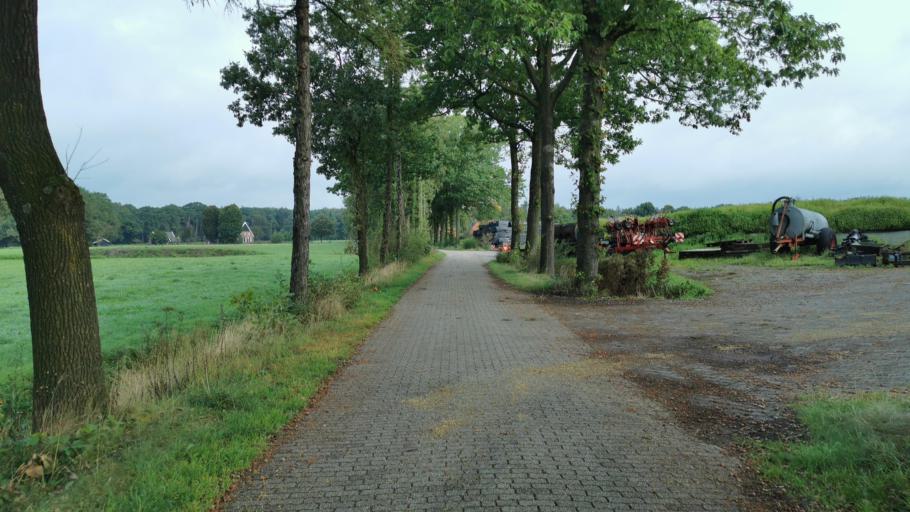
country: NL
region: Gelderland
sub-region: Gemeente Winterswijk
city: Winterswijk
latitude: 51.9250
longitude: 6.6887
